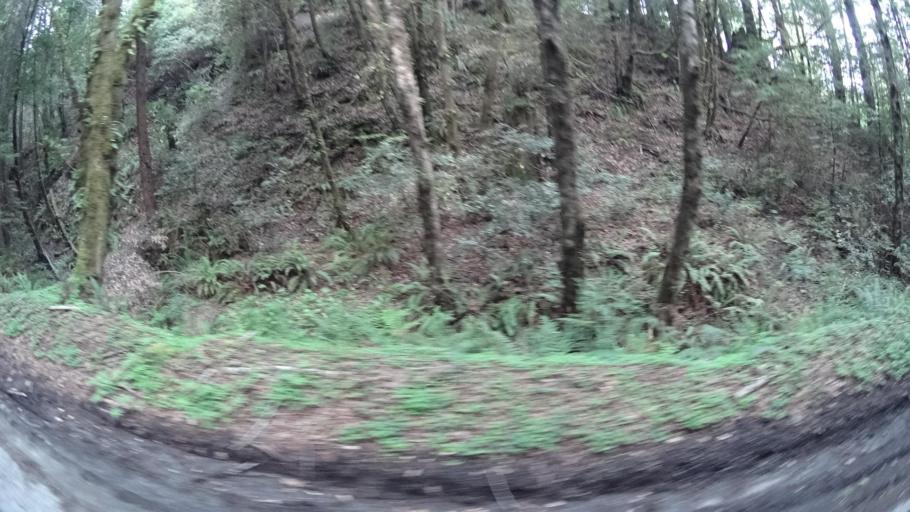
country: US
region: California
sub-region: Humboldt County
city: Redway
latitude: 40.3370
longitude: -123.9031
